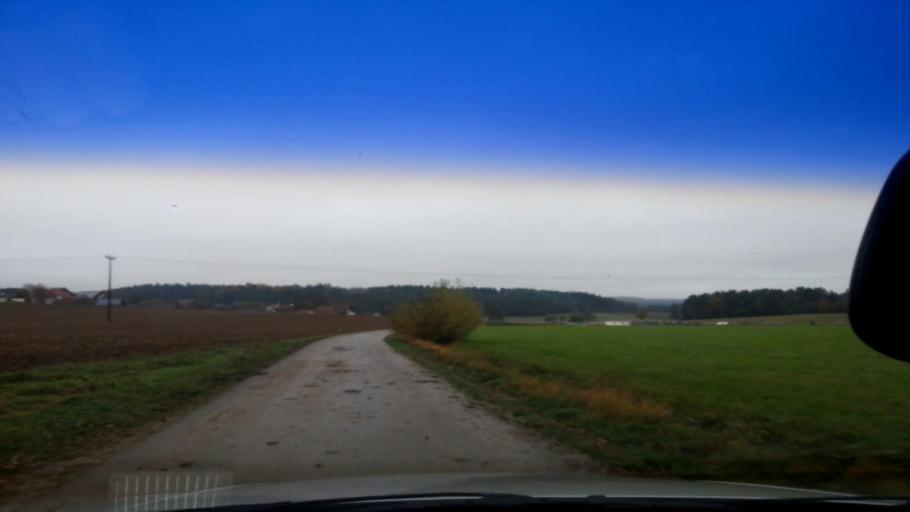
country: DE
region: Bavaria
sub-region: Upper Franconia
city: Wattendorf
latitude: 50.0329
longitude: 11.1527
